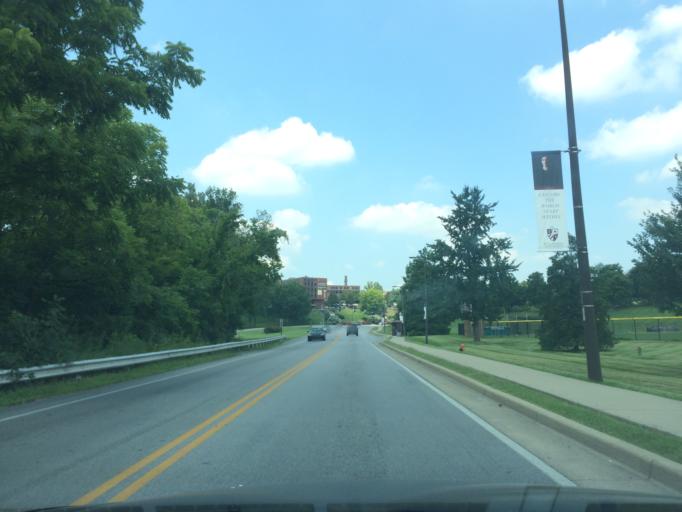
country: US
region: Kentucky
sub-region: Jefferson County
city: Audubon Park
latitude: 38.2160
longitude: -85.7054
